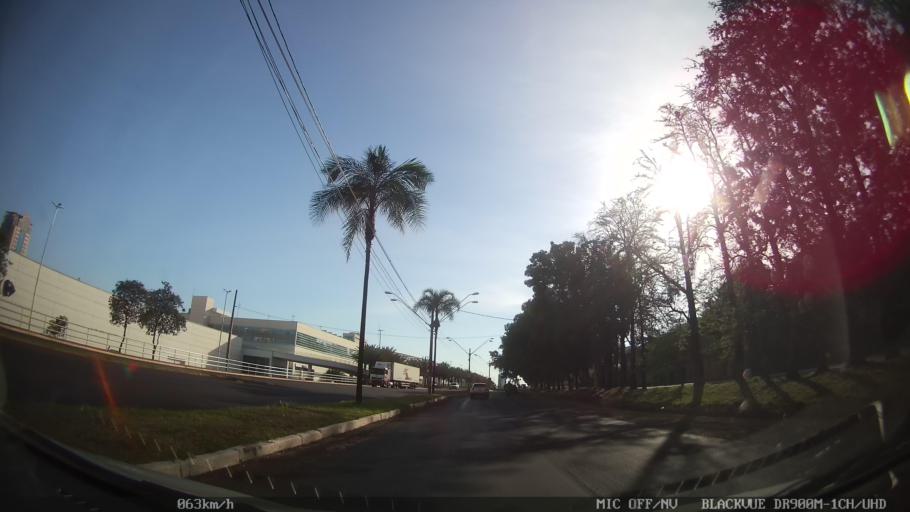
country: BR
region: Sao Paulo
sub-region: Ribeirao Preto
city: Ribeirao Preto
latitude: -21.2143
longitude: -47.8148
